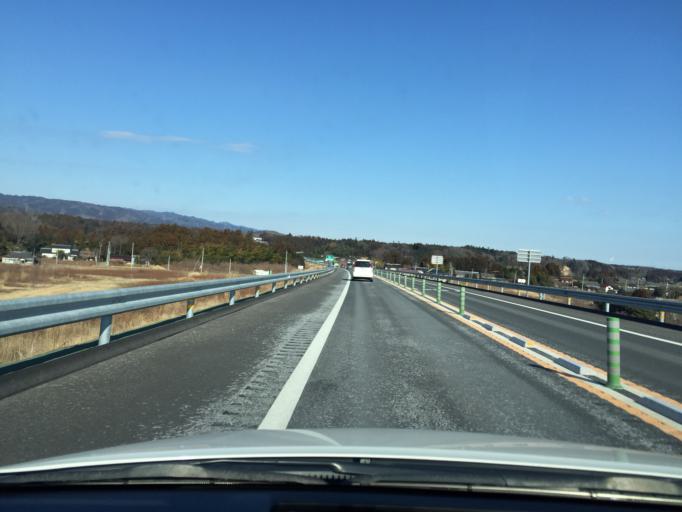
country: JP
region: Fukushima
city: Namie
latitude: 37.4688
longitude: 140.9622
